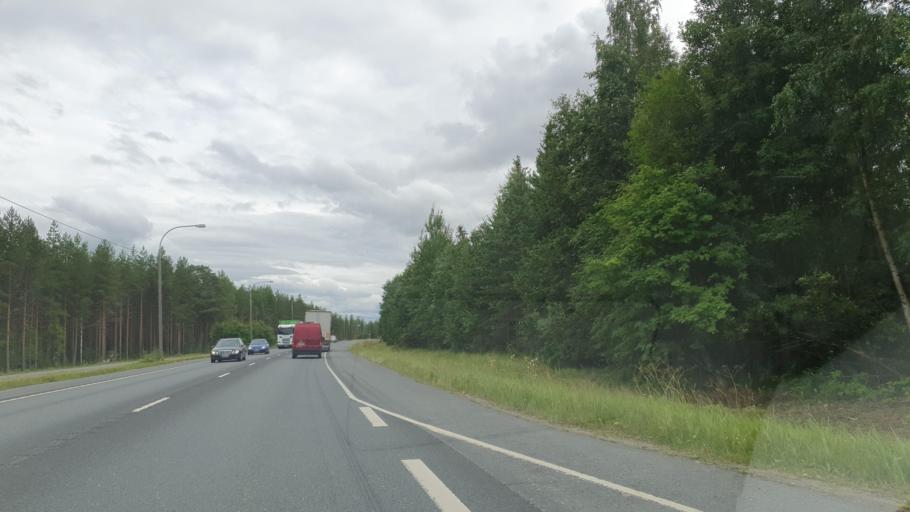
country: FI
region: Northern Savo
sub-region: Ylae-Savo
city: Iisalmi
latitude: 63.4899
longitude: 27.2819
